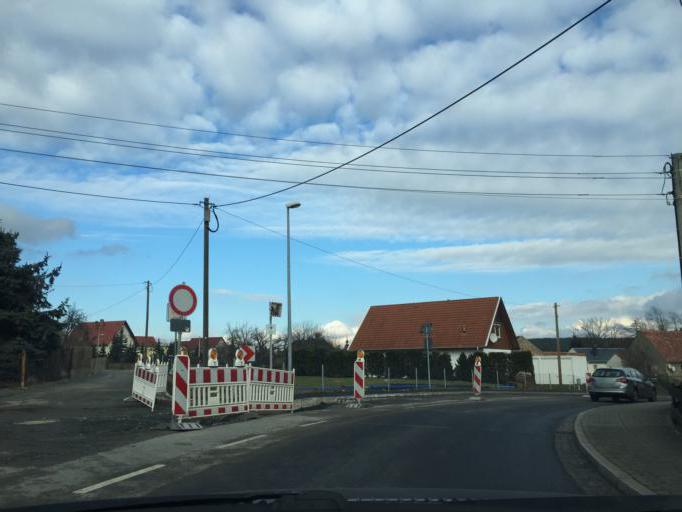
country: DE
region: Saxony
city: Radeburg
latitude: 51.1949
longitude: 13.7704
